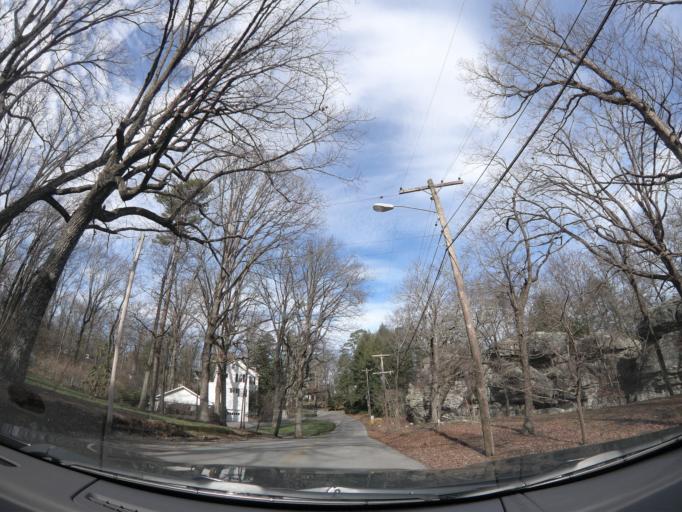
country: US
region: Georgia
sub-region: Walker County
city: Lookout Mountain
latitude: 34.9811
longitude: -85.3496
